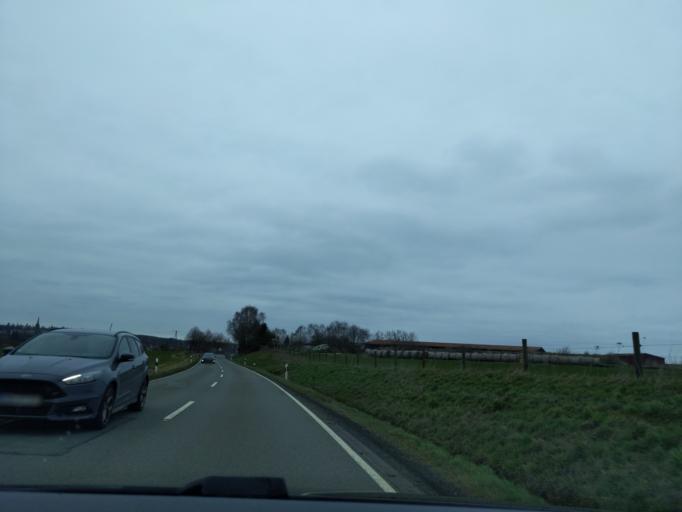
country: DE
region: Hesse
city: Frankenberg
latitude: 51.0466
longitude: 8.8177
